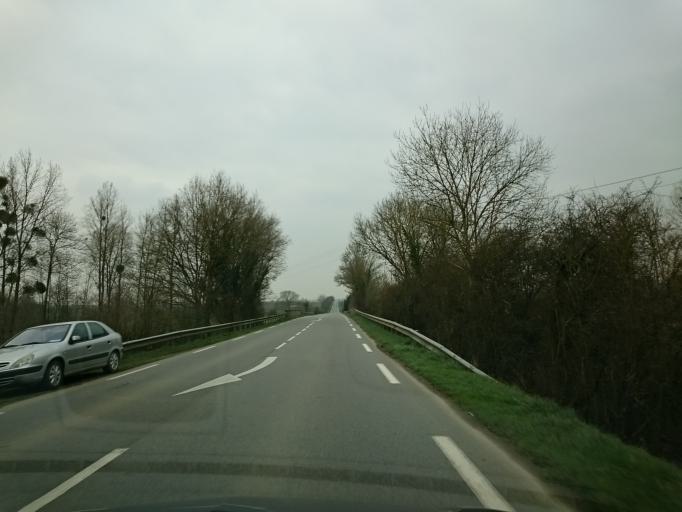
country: FR
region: Brittany
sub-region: Departement d'Ille-et-Vilaine
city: Pance
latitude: 47.8737
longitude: -1.6496
